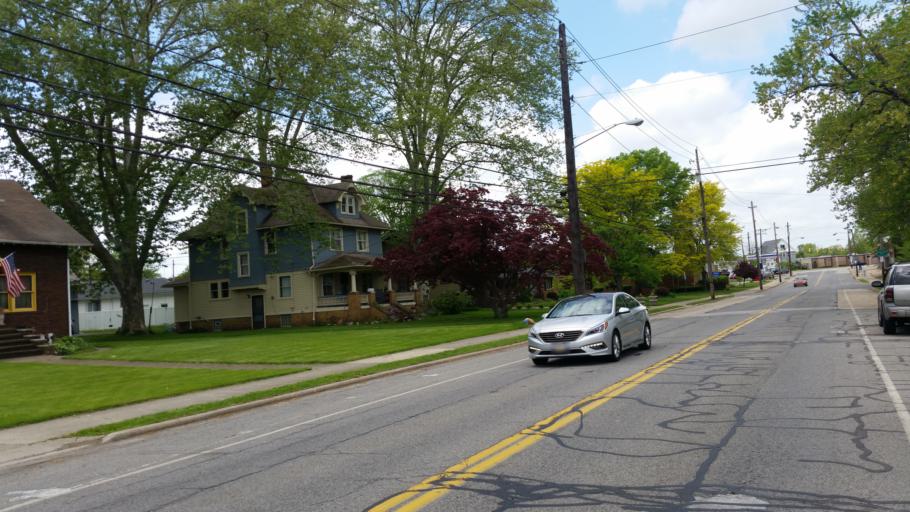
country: US
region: Ohio
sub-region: Cuyahoga County
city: Brooklyn Heights
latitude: 41.4285
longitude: -81.6947
